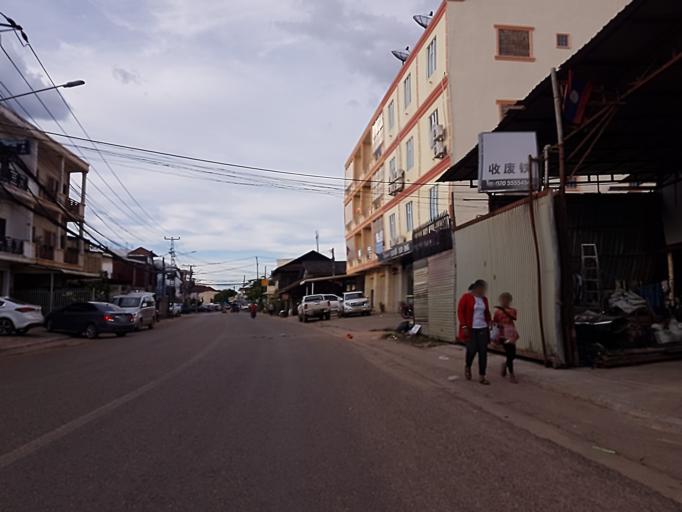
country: LA
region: Vientiane
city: Vientiane
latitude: 17.9712
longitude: 102.5970
